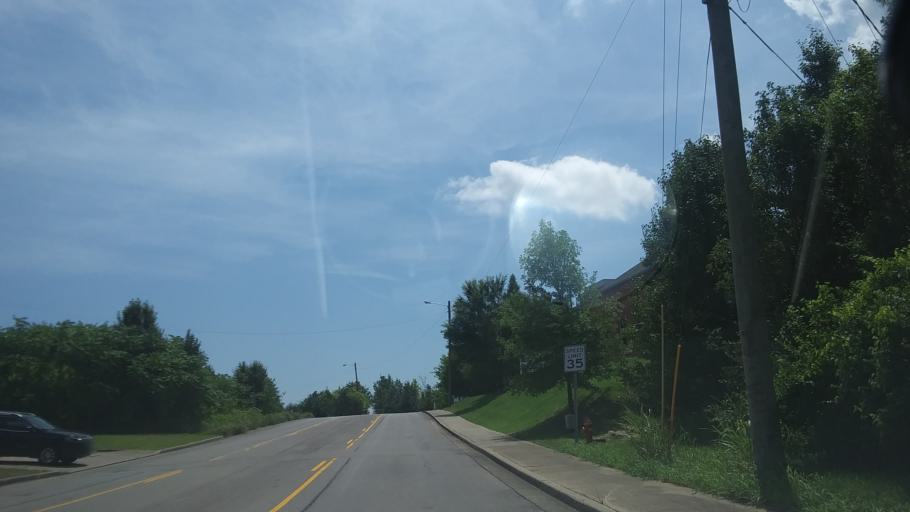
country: US
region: Tennessee
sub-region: Rutherford County
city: La Vergne
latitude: 36.0663
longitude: -86.6342
